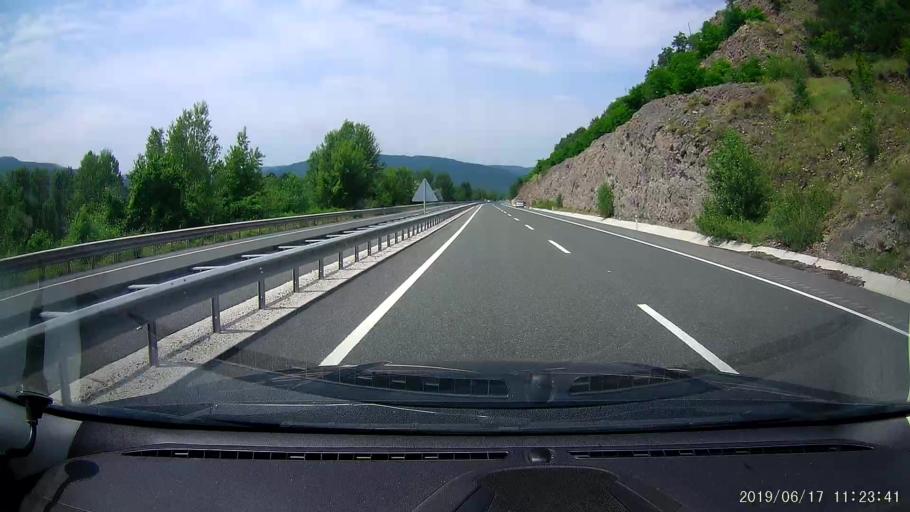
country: TR
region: Cankiri
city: Ilgaz
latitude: 40.8852
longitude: 33.7257
